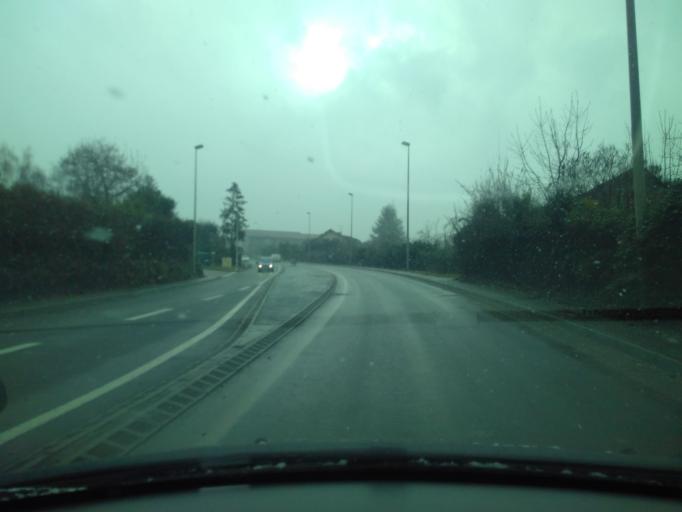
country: FR
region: Rhone-Alpes
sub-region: Departement de la Haute-Savoie
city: Saint-Julien-en-Genevois
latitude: 46.1360
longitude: 6.0791
